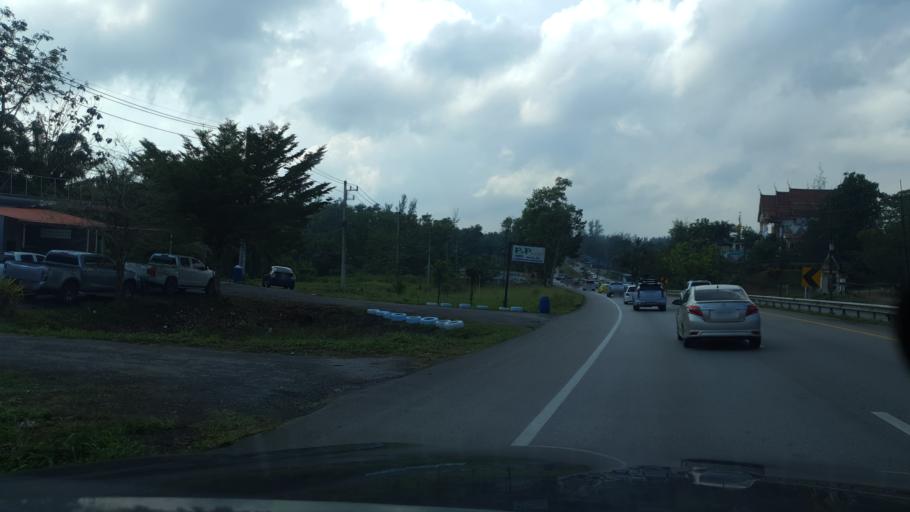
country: TH
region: Chumphon
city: Pathio
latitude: 10.8208
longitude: 99.2117
